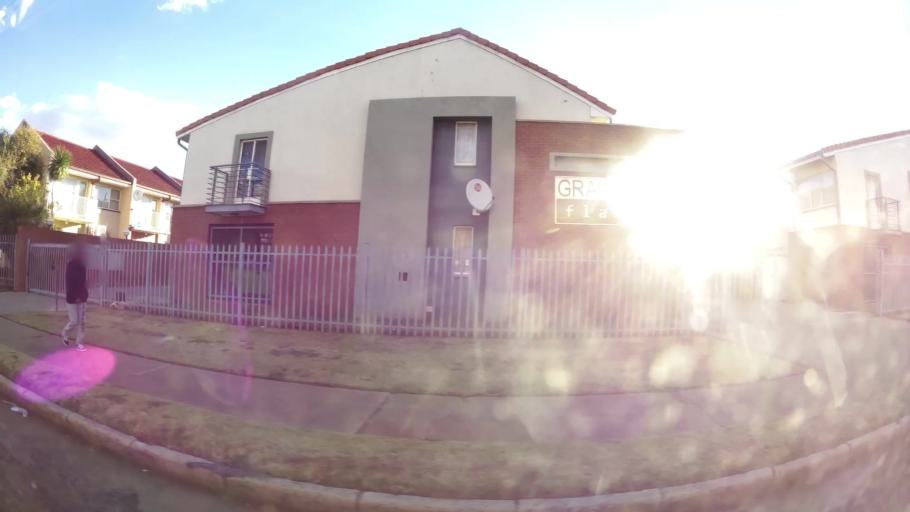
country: ZA
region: North-West
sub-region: Dr Kenneth Kaunda District Municipality
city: Potchefstroom
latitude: -26.7211
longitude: 27.0964
